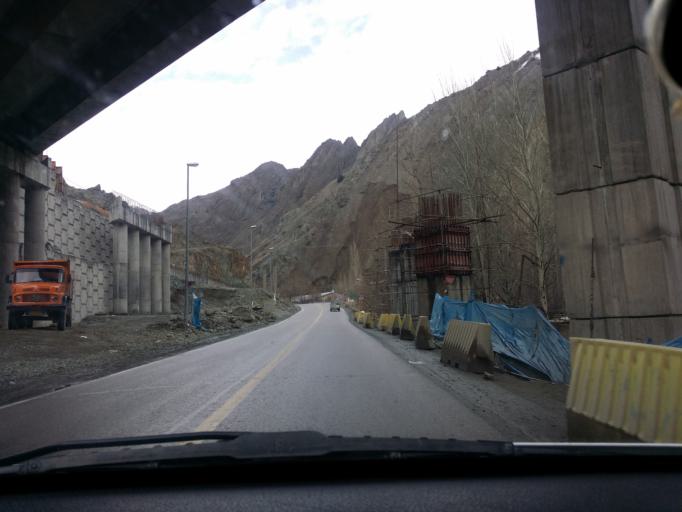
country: IR
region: Tehran
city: Tajrish
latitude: 36.0172
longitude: 51.2994
